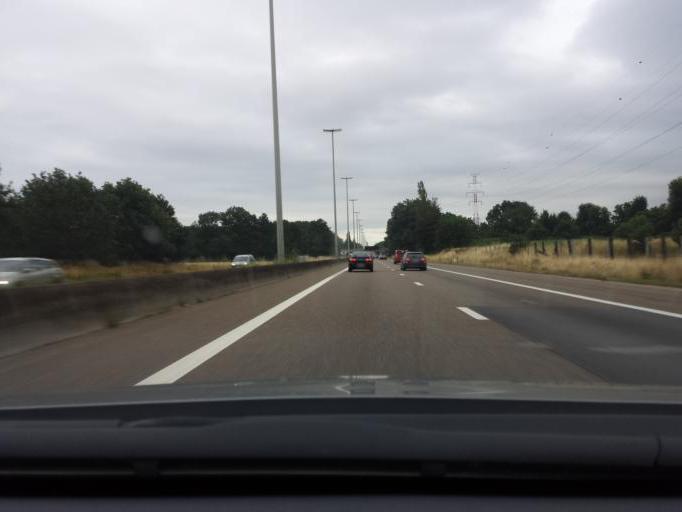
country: BE
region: Flanders
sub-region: Provincie Limburg
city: Beringen
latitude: 51.0272
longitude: 5.2023
